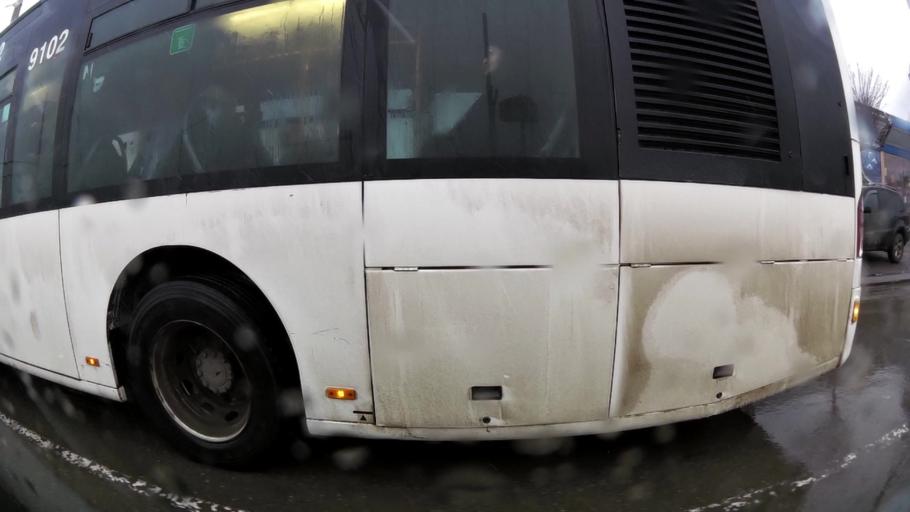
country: BG
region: Sofia-Capital
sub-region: Stolichna Obshtina
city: Sofia
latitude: 42.6546
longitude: 23.4006
